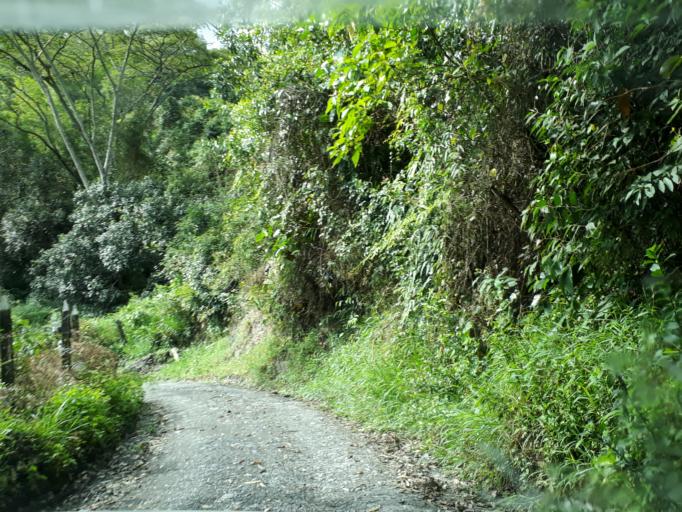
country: CO
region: Cundinamarca
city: Pacho
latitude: 5.1695
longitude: -74.2423
